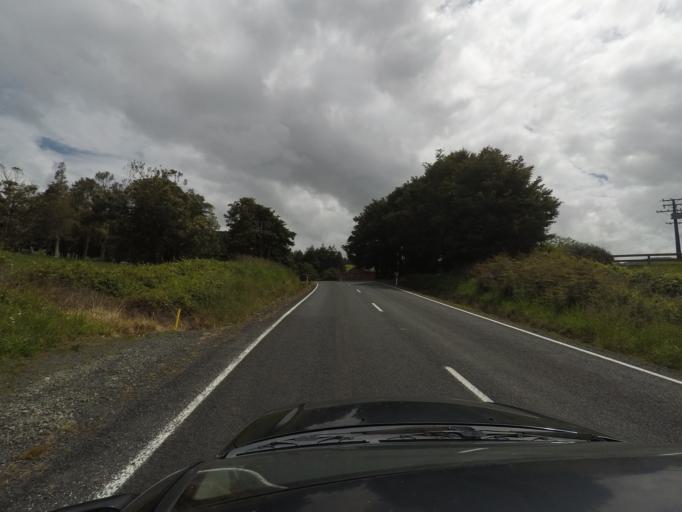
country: NZ
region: Auckland
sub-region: Auckland
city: Parakai
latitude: -36.5026
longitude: 174.5104
